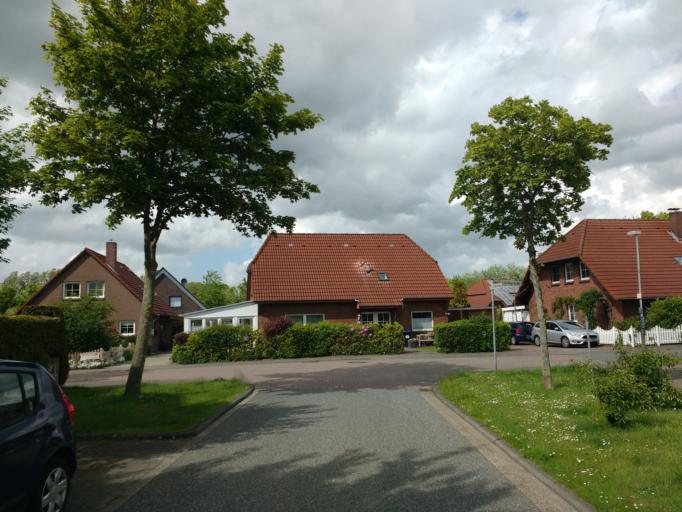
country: DE
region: Lower Saxony
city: Jever
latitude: 53.5804
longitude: 7.9115
